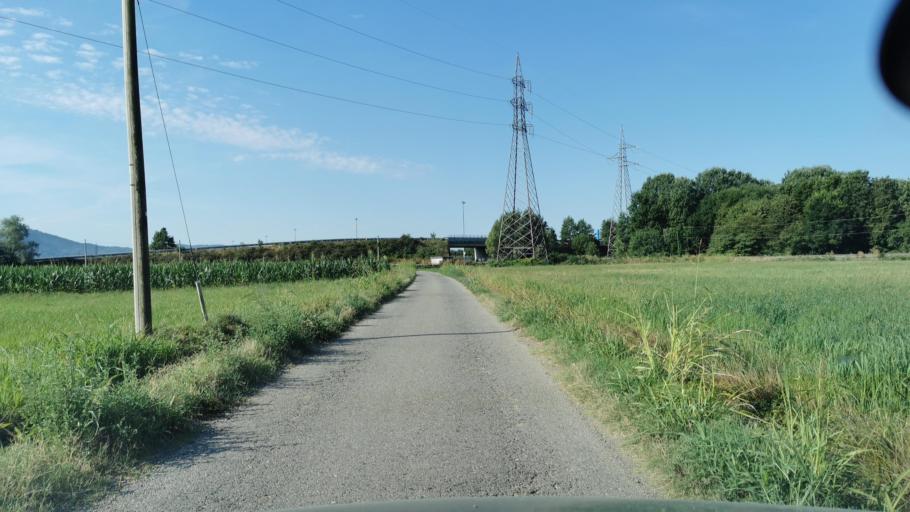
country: IT
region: Piedmont
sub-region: Provincia di Torino
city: Settimo Torinese
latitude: 45.1622
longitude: 7.7749
